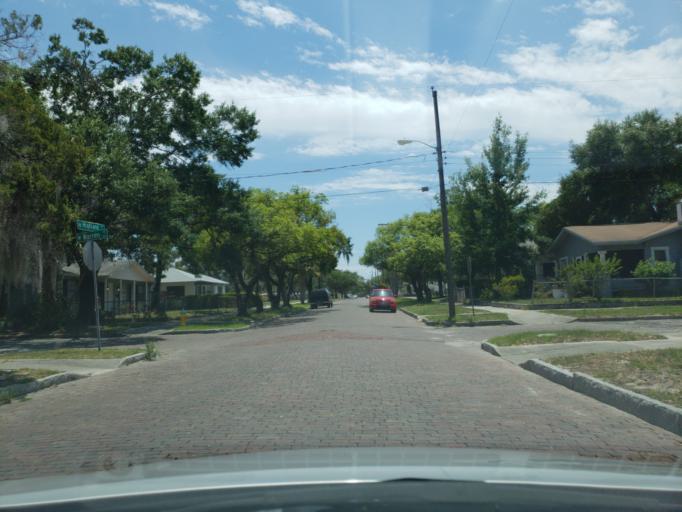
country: US
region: Florida
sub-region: Hillsborough County
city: Tampa
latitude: 27.9693
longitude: -82.4623
